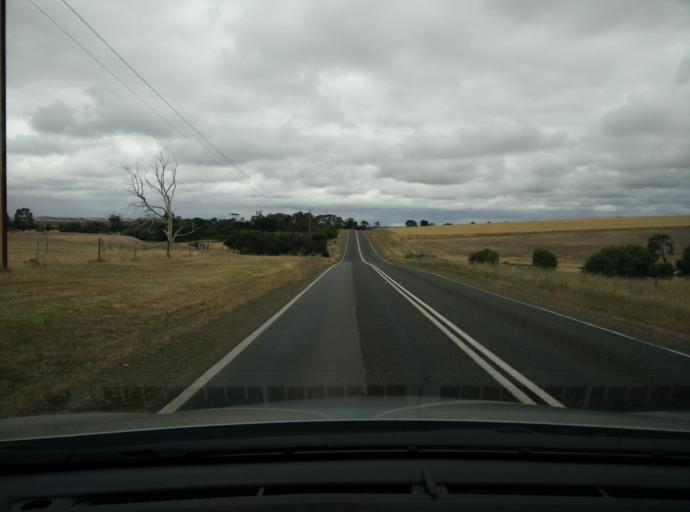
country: AU
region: South Australia
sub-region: Kangaroo Island
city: Kingscote
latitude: -35.6684
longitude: 137.5948
